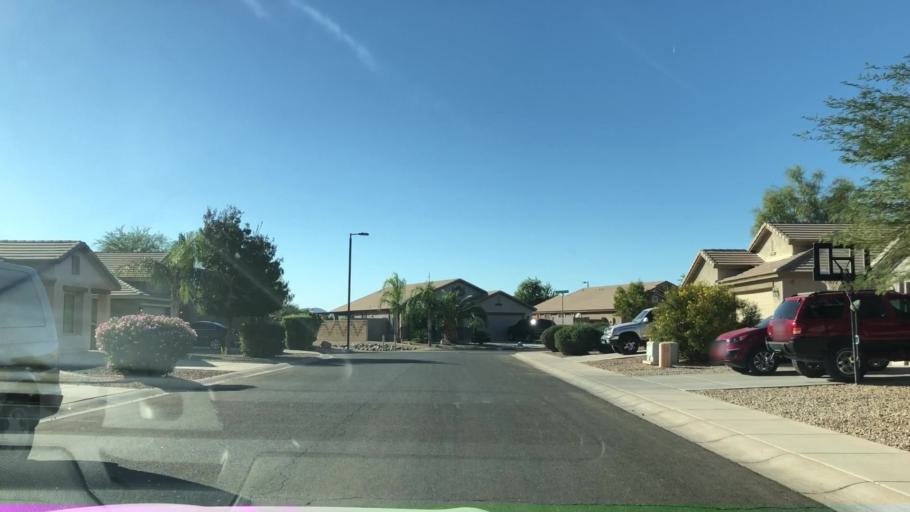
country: US
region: Arizona
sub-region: Pinal County
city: San Tan Valley
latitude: 33.1587
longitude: -111.5348
